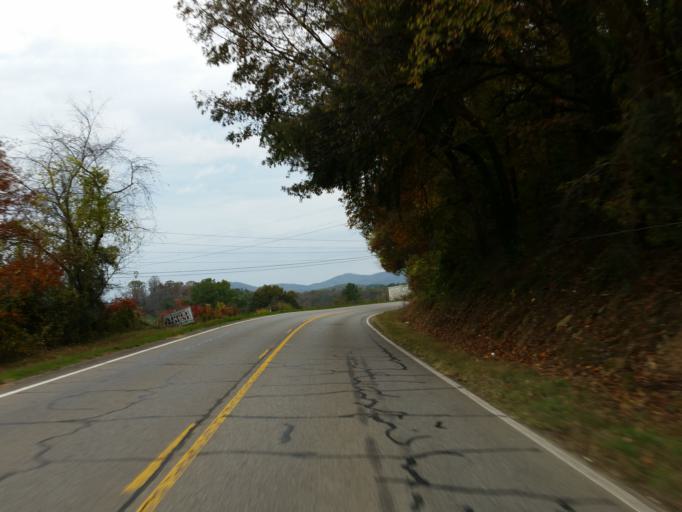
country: US
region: Georgia
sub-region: Gilmer County
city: Ellijay
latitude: 34.6314
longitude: -84.3870
